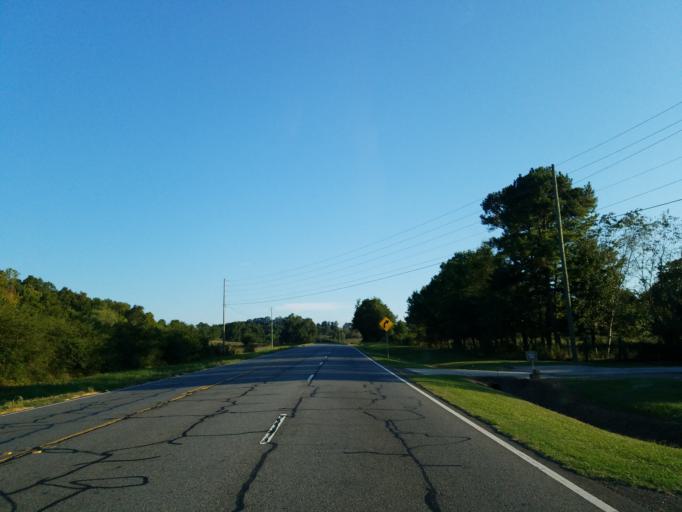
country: US
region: Georgia
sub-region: Bartow County
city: Rydal
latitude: 34.3916
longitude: -84.7066
